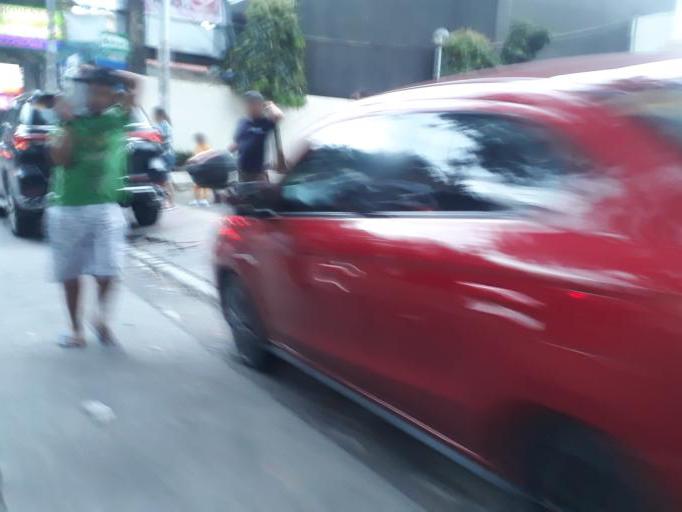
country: PH
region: Metro Manila
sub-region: Quezon City
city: Quezon City
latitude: 14.6794
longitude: 121.0811
